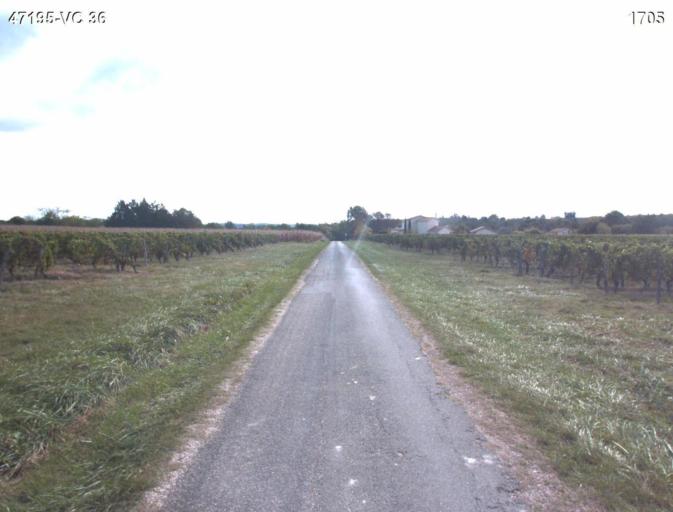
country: FR
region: Aquitaine
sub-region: Departement du Lot-et-Garonne
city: Nerac
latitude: 44.1236
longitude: 0.3287
